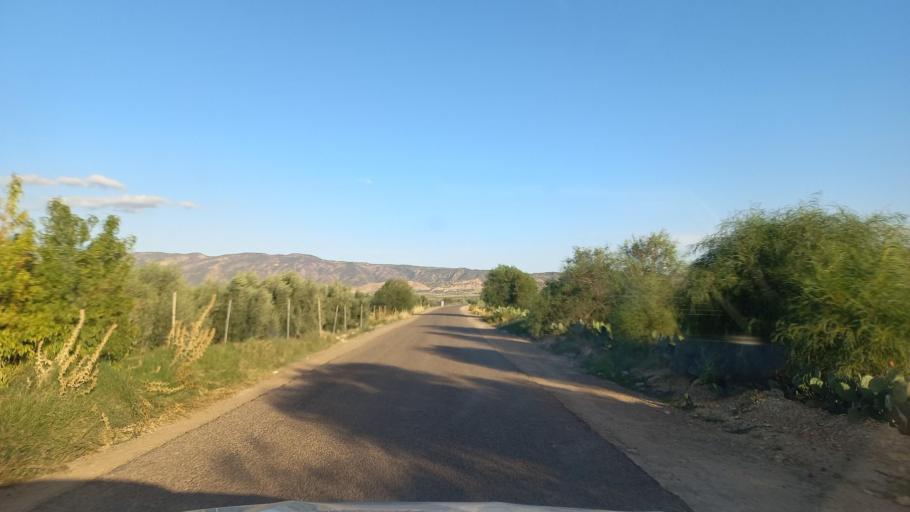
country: TN
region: Al Qasrayn
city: Sbiba
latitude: 35.4131
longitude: 9.1255
